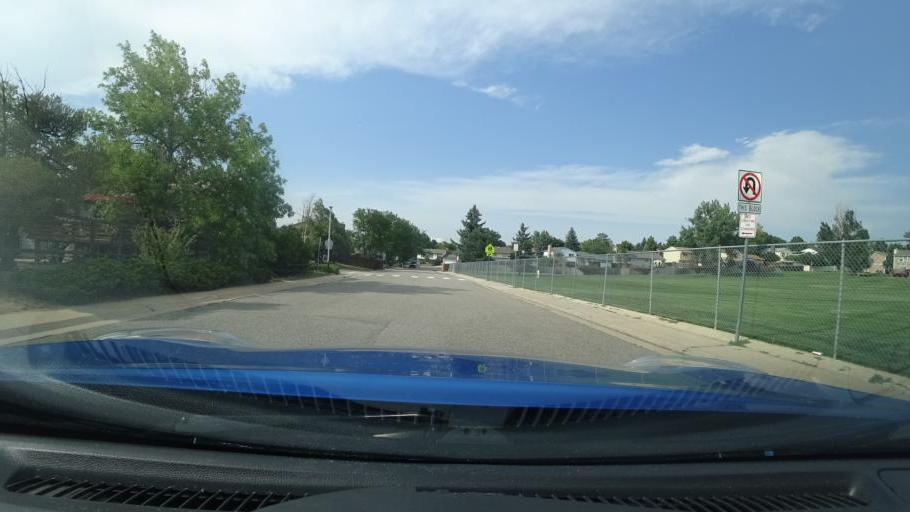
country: US
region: Colorado
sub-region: Adams County
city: Aurora
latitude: 39.6885
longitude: -104.7942
